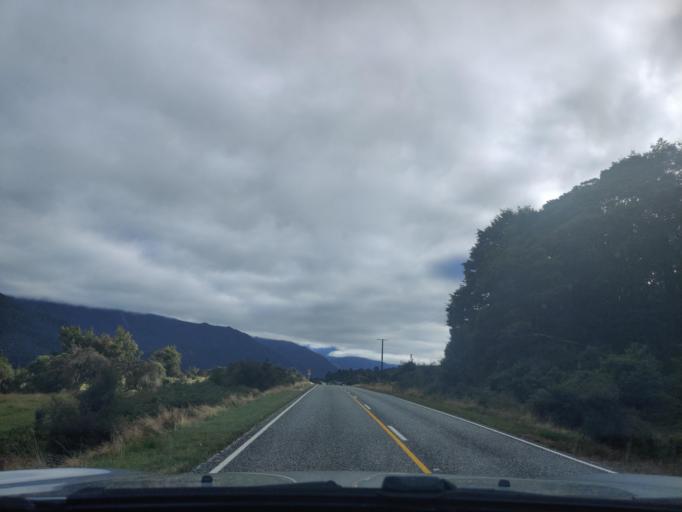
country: NZ
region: Otago
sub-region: Queenstown-Lakes District
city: Wanaka
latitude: -44.2396
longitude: 169.2281
